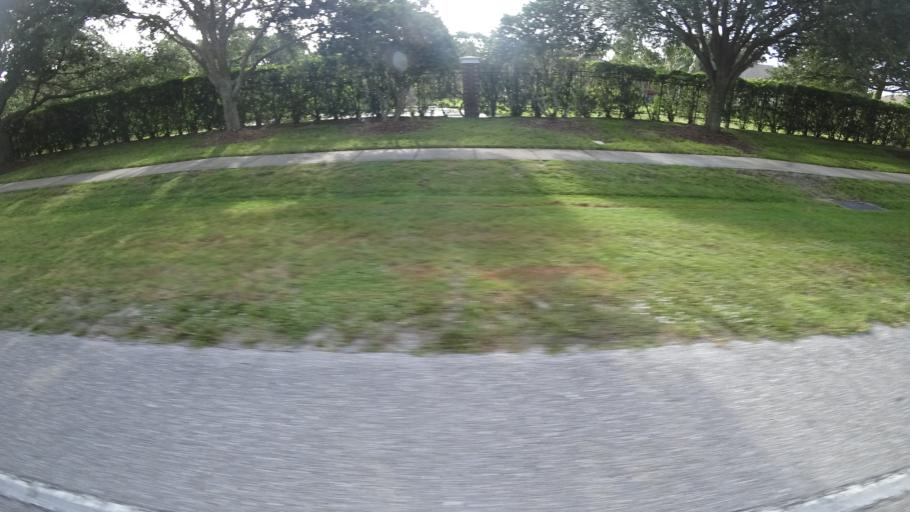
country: US
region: Florida
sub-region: Sarasota County
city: Desoto Lakes
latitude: 27.4051
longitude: -82.4630
